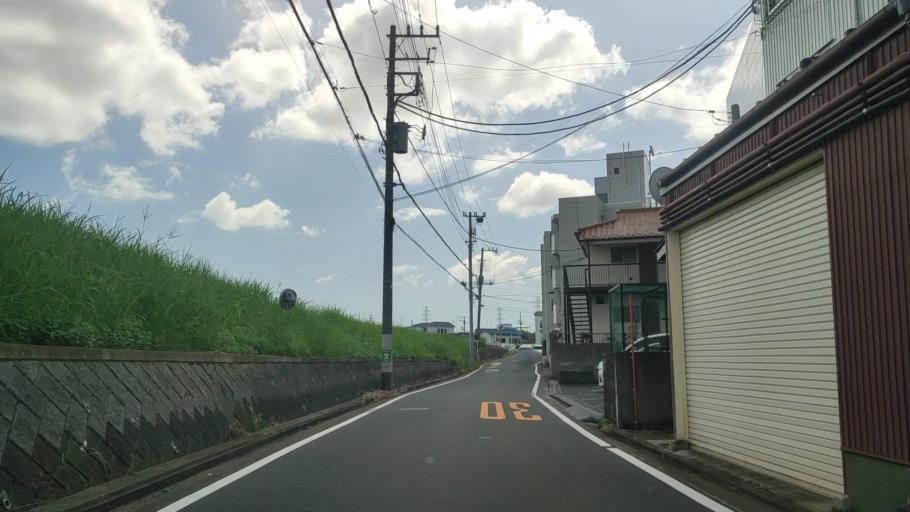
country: JP
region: Kanagawa
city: Yokohama
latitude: 35.5341
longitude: 139.6231
